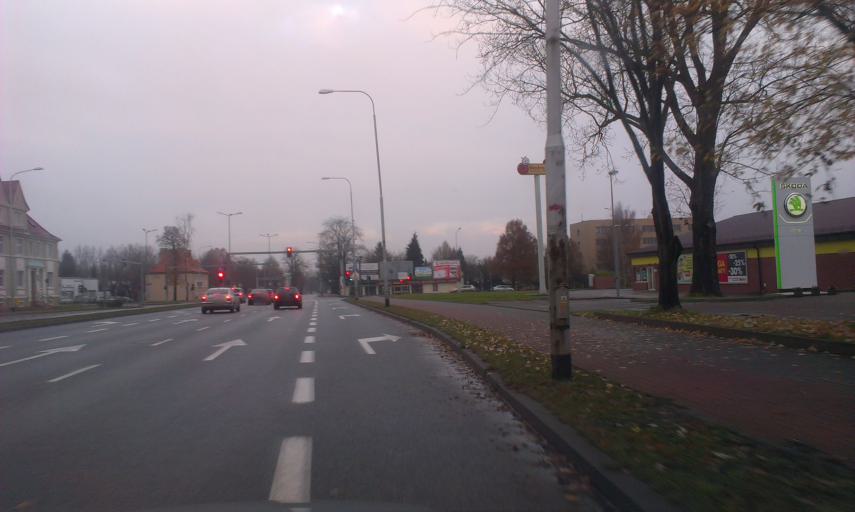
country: PL
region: West Pomeranian Voivodeship
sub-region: Koszalin
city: Koszalin
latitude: 54.1778
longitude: 16.1973
